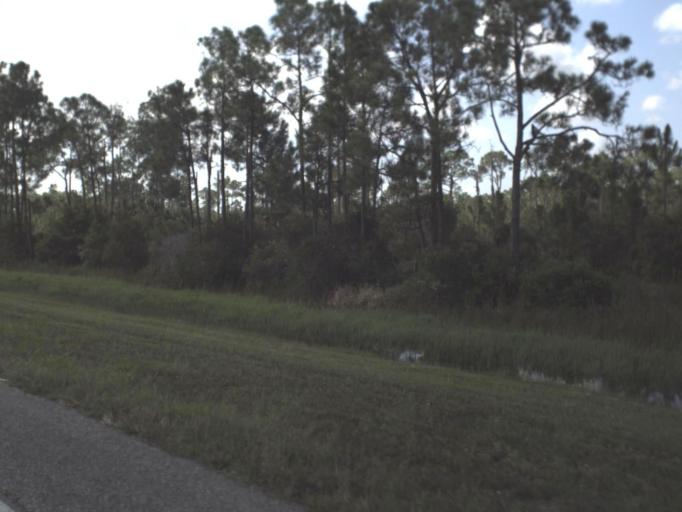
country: US
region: Florida
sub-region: Lee County
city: Burnt Store Marina
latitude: 26.8090
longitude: -81.9565
